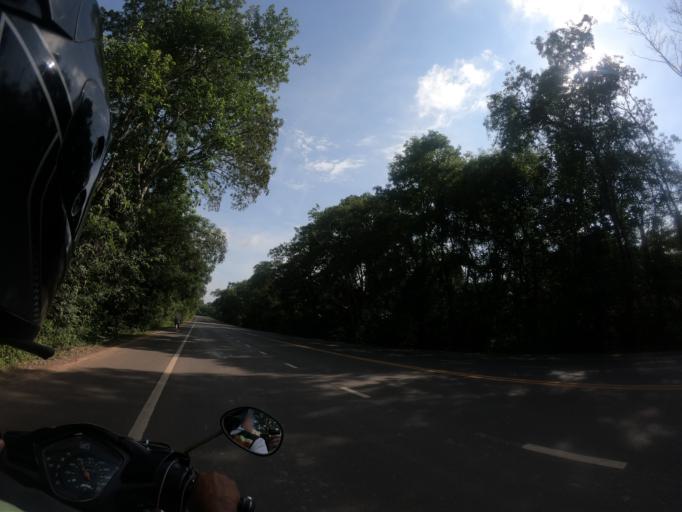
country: TH
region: Surin
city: Kap Choeng
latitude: 14.4447
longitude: 103.7007
